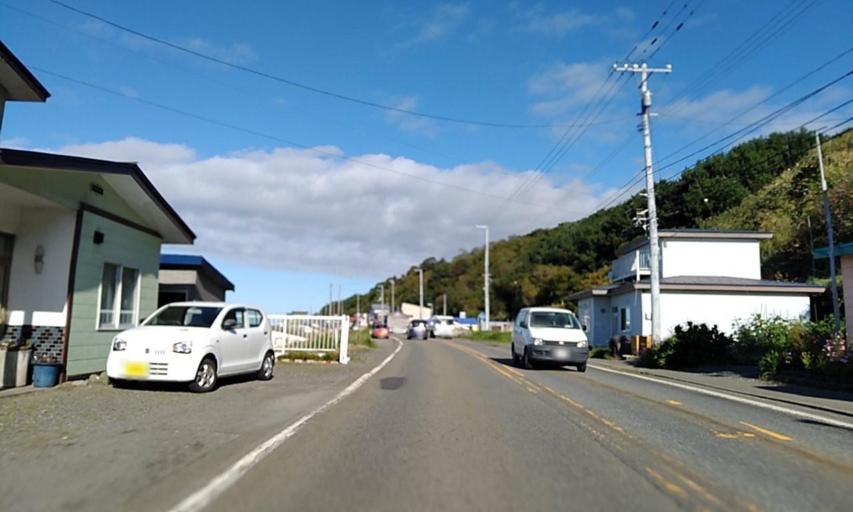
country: JP
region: Hokkaido
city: Shizunai-furukawacho
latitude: 42.2671
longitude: 142.4930
